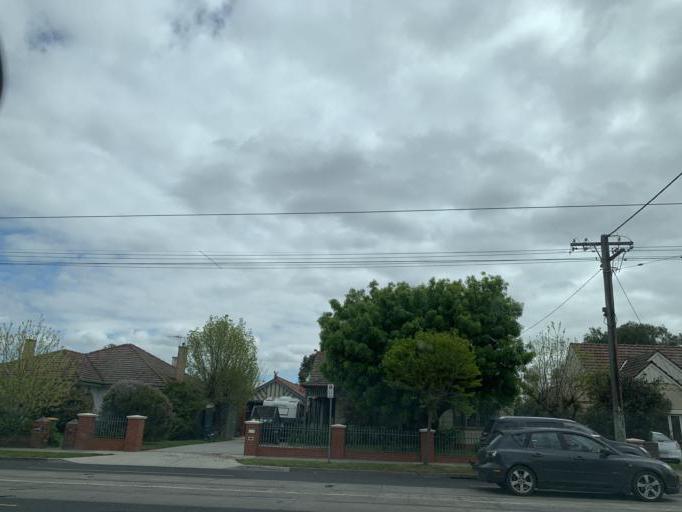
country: AU
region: Victoria
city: Thornbury
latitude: -37.7421
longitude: 144.9896
